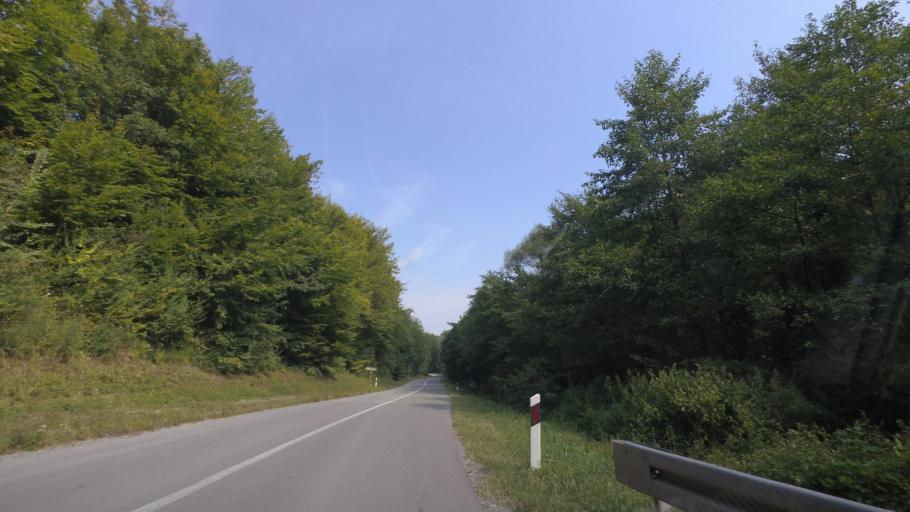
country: BA
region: Federation of Bosnia and Herzegovina
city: Zboriste
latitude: 45.2115
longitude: 16.1301
